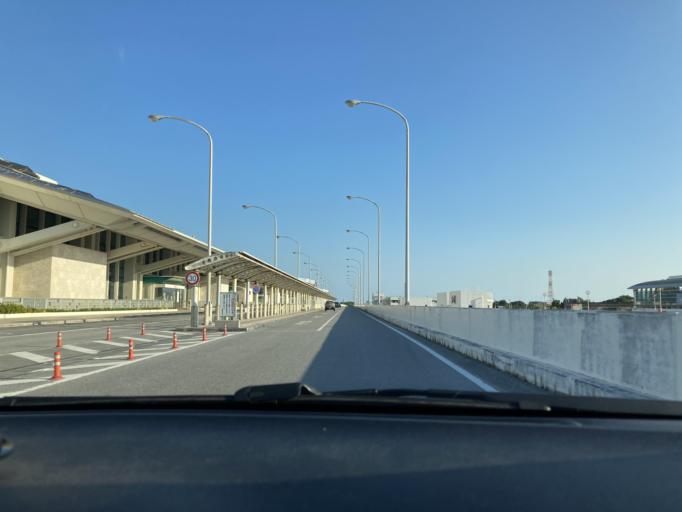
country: JP
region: Okinawa
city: Naha-shi
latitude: 26.2052
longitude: 127.6513
